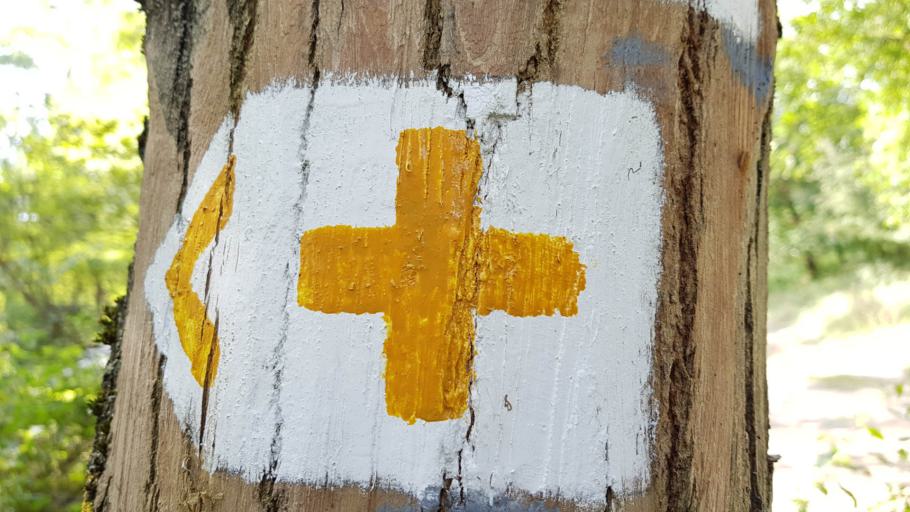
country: HU
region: Somogy
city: Nagybajom
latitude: 46.5089
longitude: 17.5067
